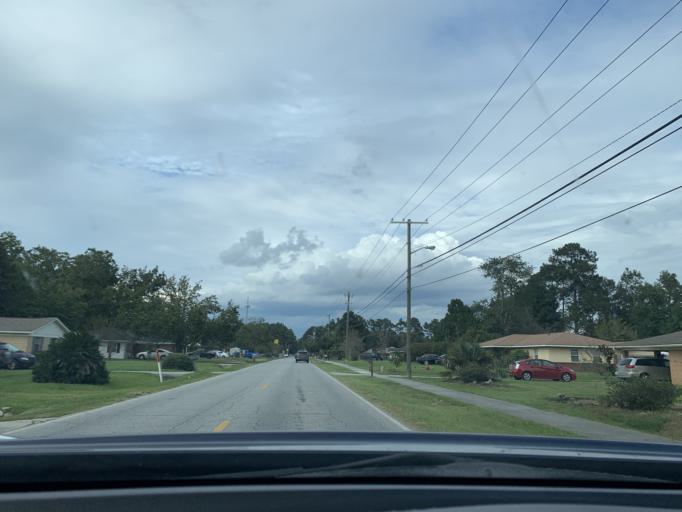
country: US
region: Georgia
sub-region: Chatham County
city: Pooler
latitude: 32.1037
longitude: -81.2531
